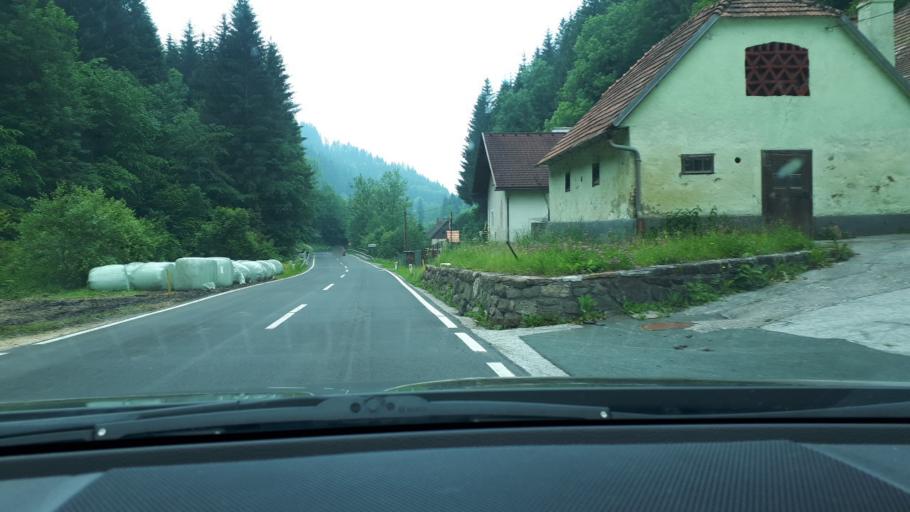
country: AT
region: Carinthia
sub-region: Politischer Bezirk Wolfsberg
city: Preitenegg
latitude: 46.9300
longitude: 14.8919
